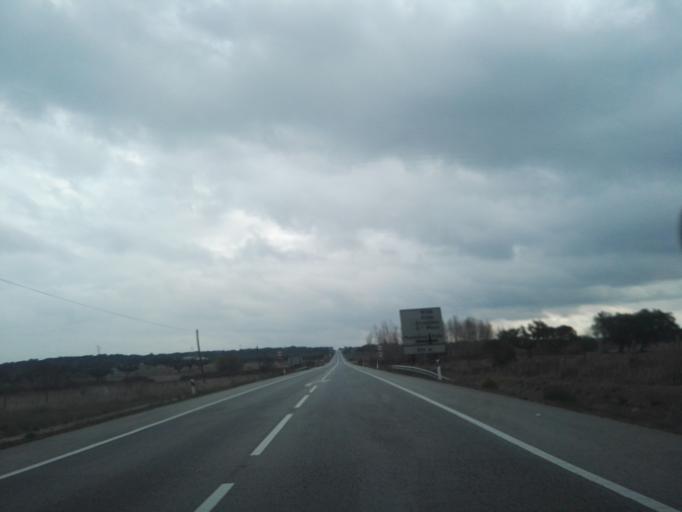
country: PT
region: Portalegre
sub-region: Arronches
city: Arronches
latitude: 39.1625
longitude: -7.3235
